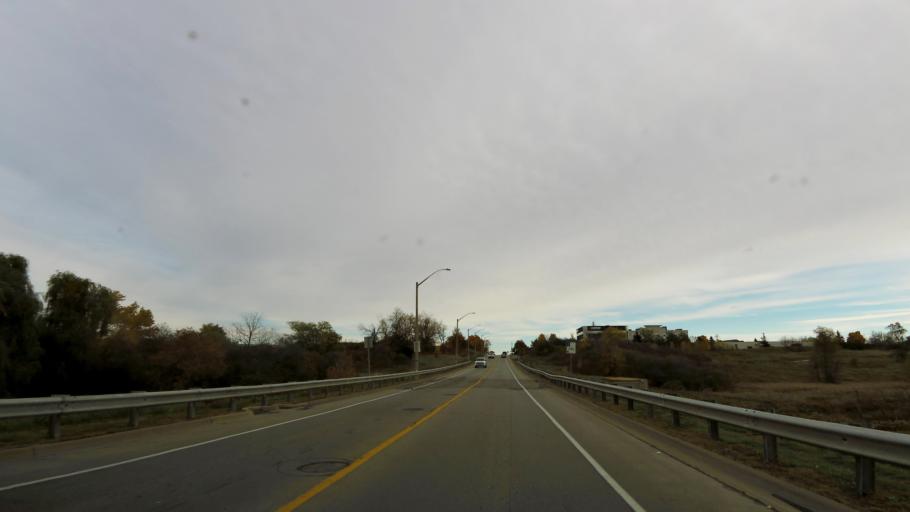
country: CA
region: Ontario
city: Hamilton
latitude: 43.1960
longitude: -79.8271
